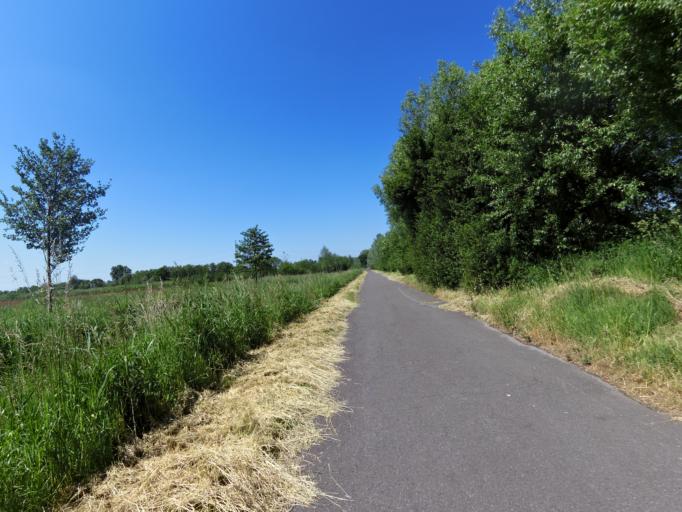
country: DE
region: North Rhine-Westphalia
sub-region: Regierungsbezirk Koln
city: Gangelt
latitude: 50.9824
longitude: 5.9893
